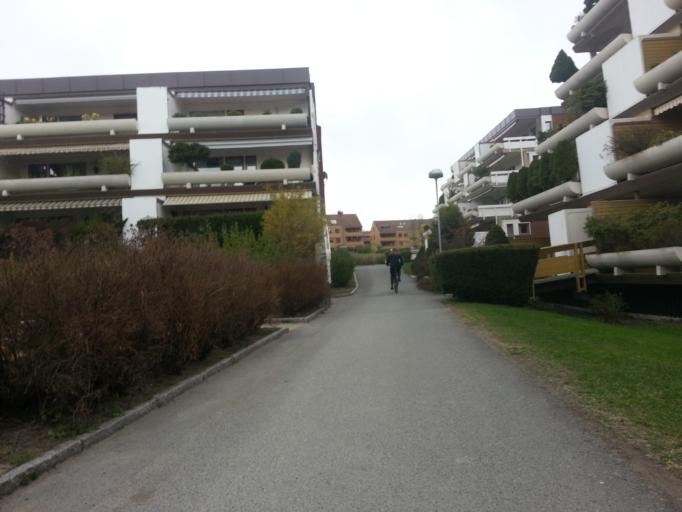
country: NO
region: Oslo
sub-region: Oslo
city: Sjolyststranda
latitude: 59.9264
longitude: 10.6838
